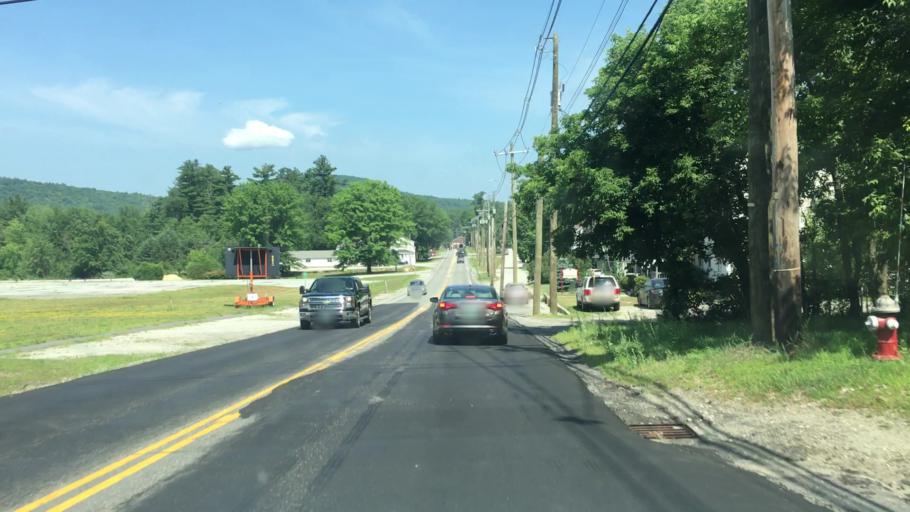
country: US
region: New Hampshire
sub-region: Sullivan County
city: Newport
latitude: 43.3754
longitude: -72.1372
